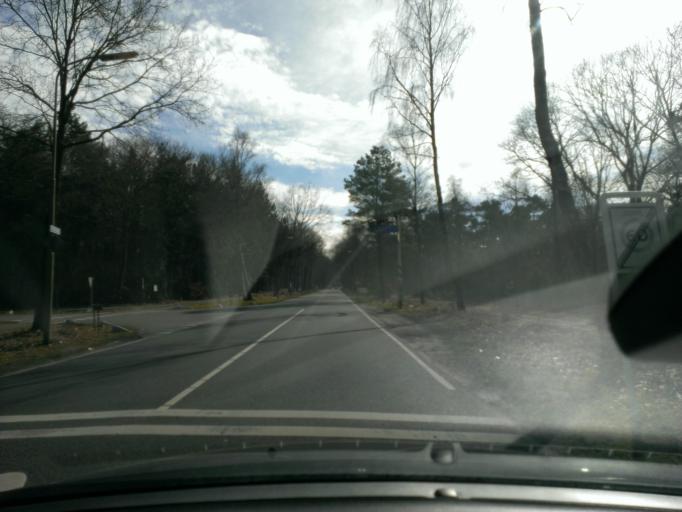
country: NL
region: Gelderland
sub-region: Gemeente Heerde
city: Heerde
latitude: 52.4409
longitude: 6.0124
